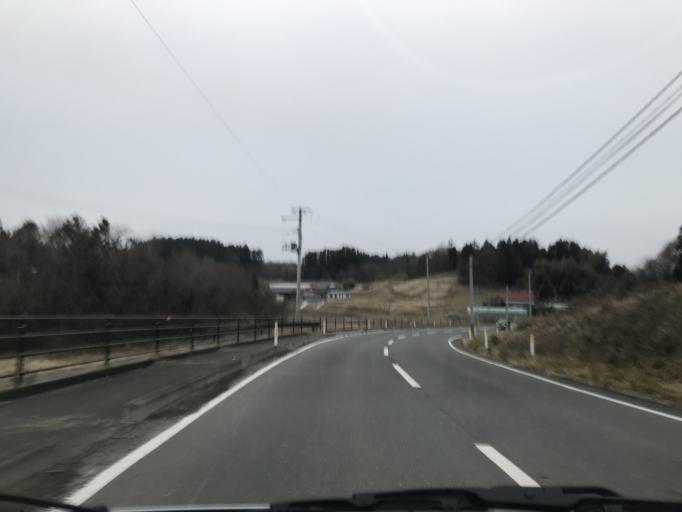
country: JP
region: Miyagi
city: Wakuya
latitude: 38.6772
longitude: 141.1008
